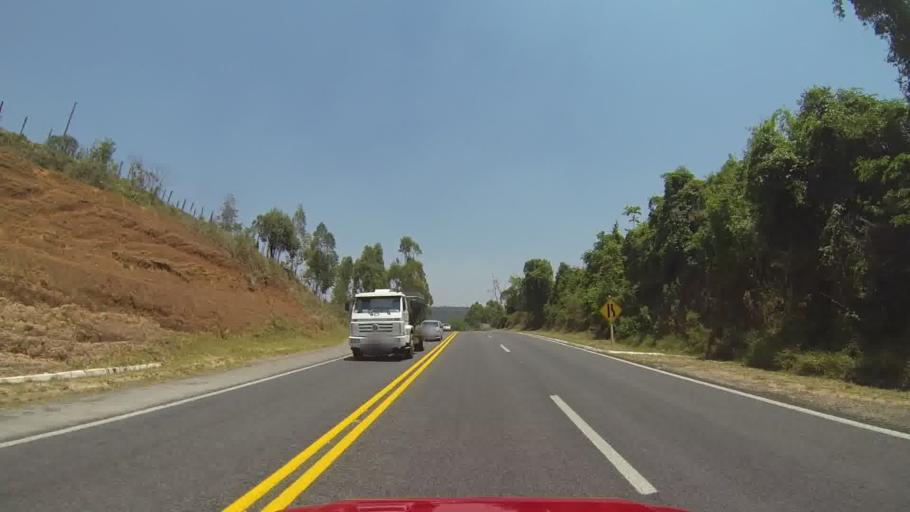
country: BR
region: Minas Gerais
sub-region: Itapecerica
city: Itapecerica
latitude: -20.2942
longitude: -45.1744
